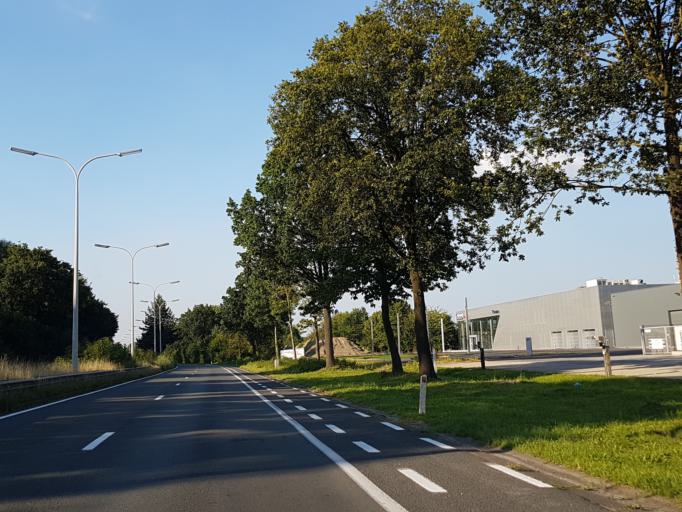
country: BE
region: Flanders
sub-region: Provincie Oost-Vlaanderen
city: Aalst
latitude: 50.9599
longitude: 4.0363
